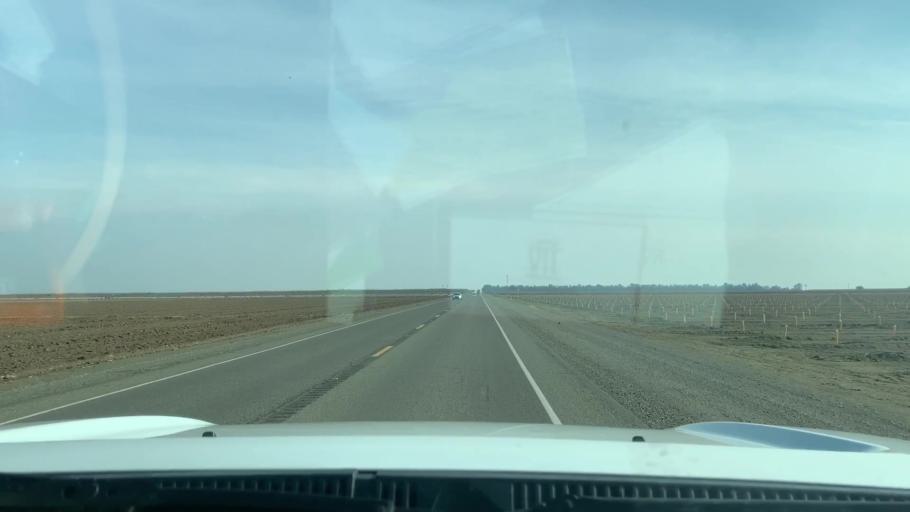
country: US
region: California
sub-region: Fresno County
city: Huron
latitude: 36.2551
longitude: -120.1896
